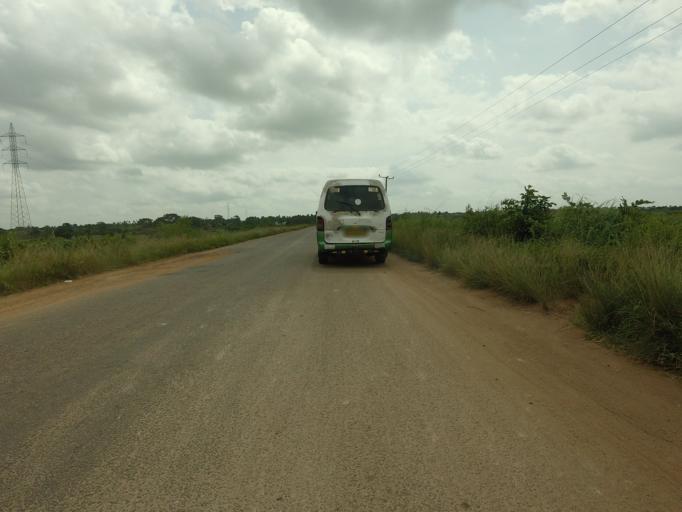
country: TG
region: Maritime
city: Lome
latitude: 6.1696
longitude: 1.0827
